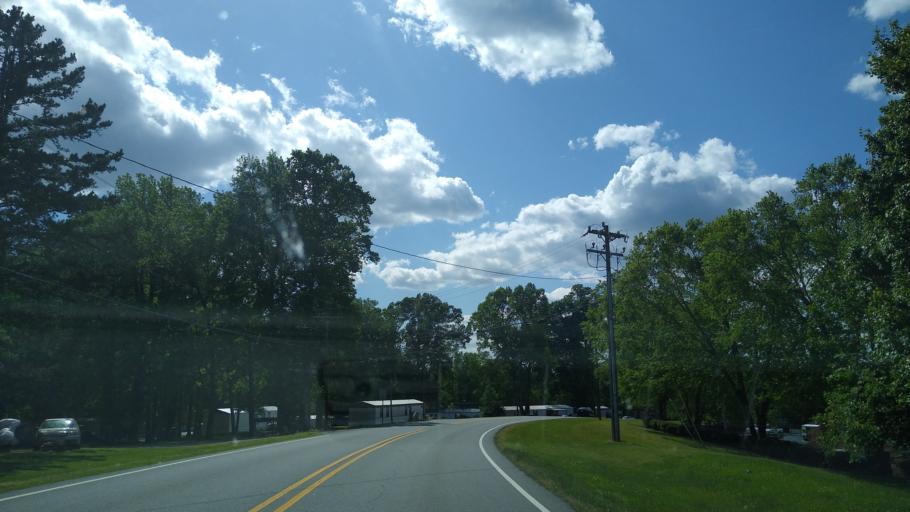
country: US
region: North Carolina
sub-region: Forsyth County
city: Kernersville
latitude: 36.0943
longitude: -80.0661
